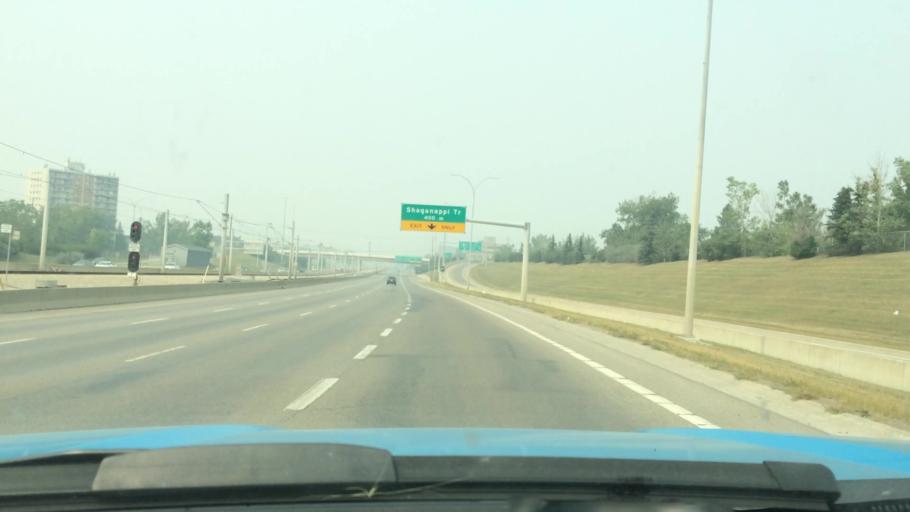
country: CA
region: Alberta
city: Calgary
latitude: 51.0912
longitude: -114.1376
